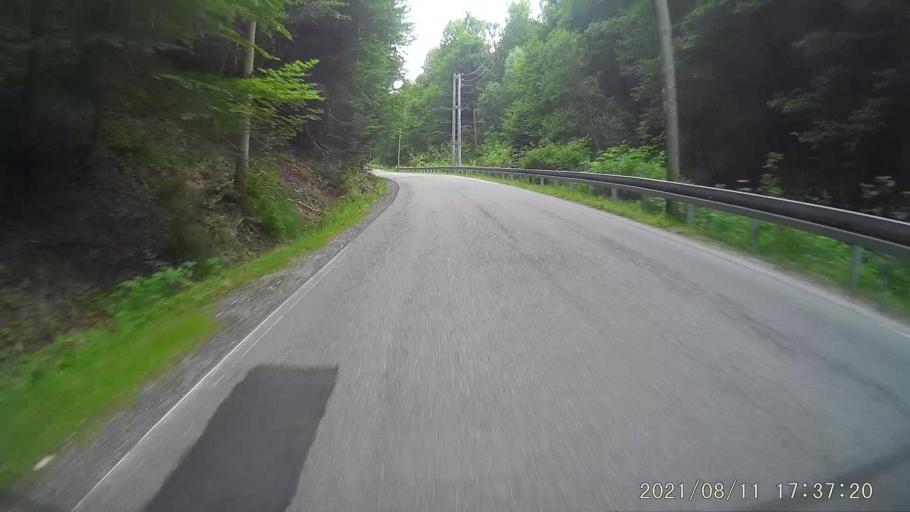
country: PL
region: Lower Silesian Voivodeship
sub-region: Powiat klodzki
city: Duszniki-Zdroj
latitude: 50.3376
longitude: 16.4050
